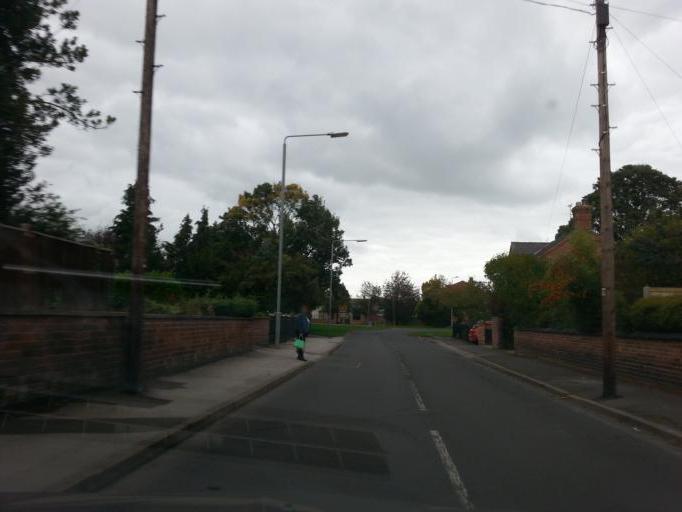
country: GB
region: England
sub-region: Nottinghamshire
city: Newark on Trent
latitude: 53.0565
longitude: -0.7785
